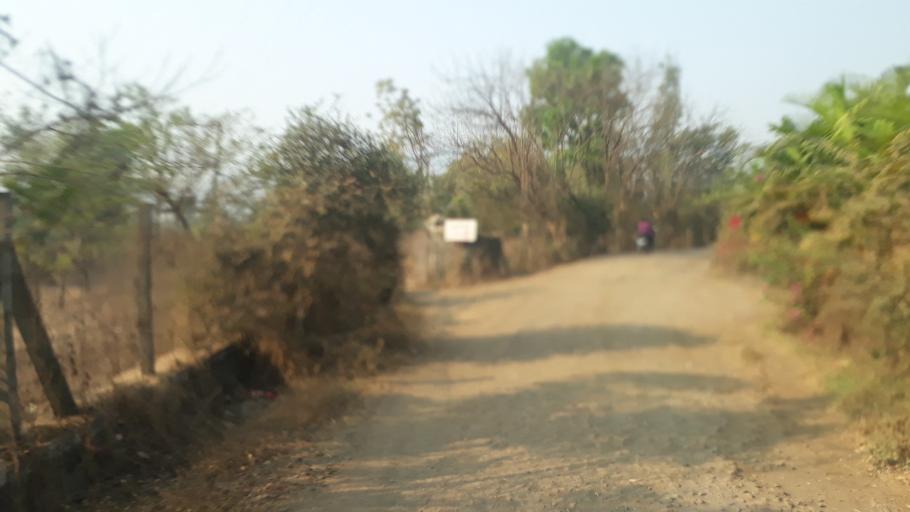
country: IN
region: Maharashtra
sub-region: Raigarh
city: Neral
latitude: 19.0438
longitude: 73.3280
